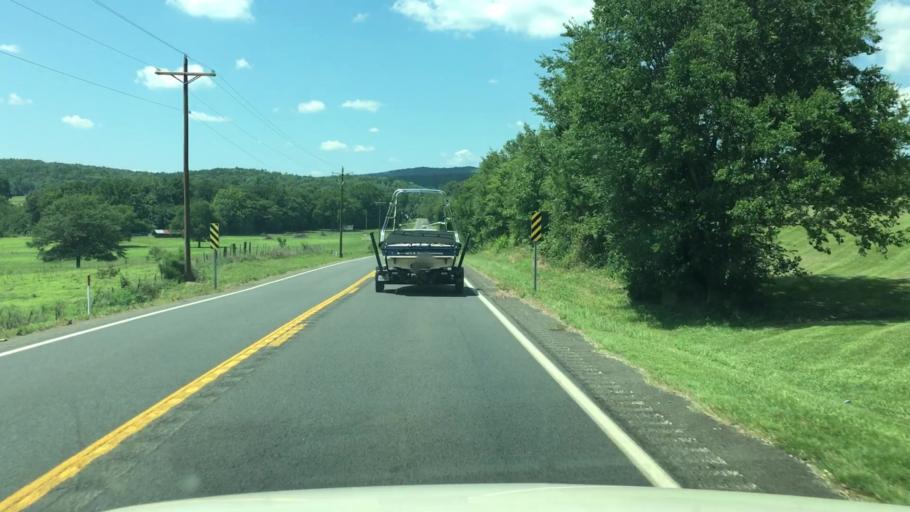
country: US
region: Arkansas
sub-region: Garland County
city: Lake Hamilton
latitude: 34.3323
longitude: -93.1762
